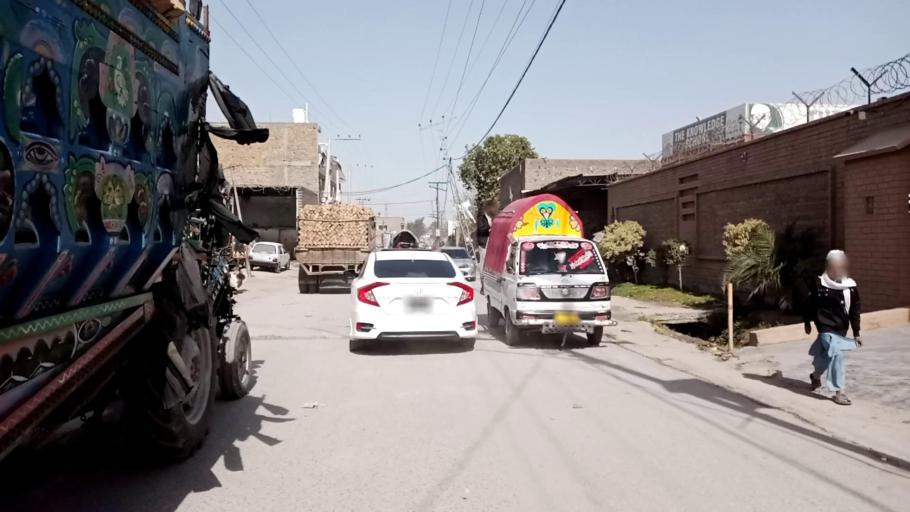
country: PK
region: Khyber Pakhtunkhwa
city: Peshawar
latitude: 34.0116
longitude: 71.6474
